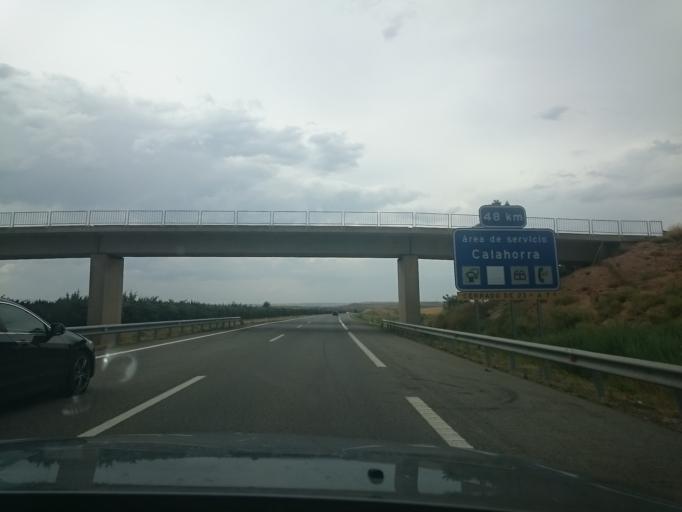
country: ES
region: Navarre
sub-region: Provincia de Navarra
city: Fontellas
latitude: 41.9951
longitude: -1.5794
